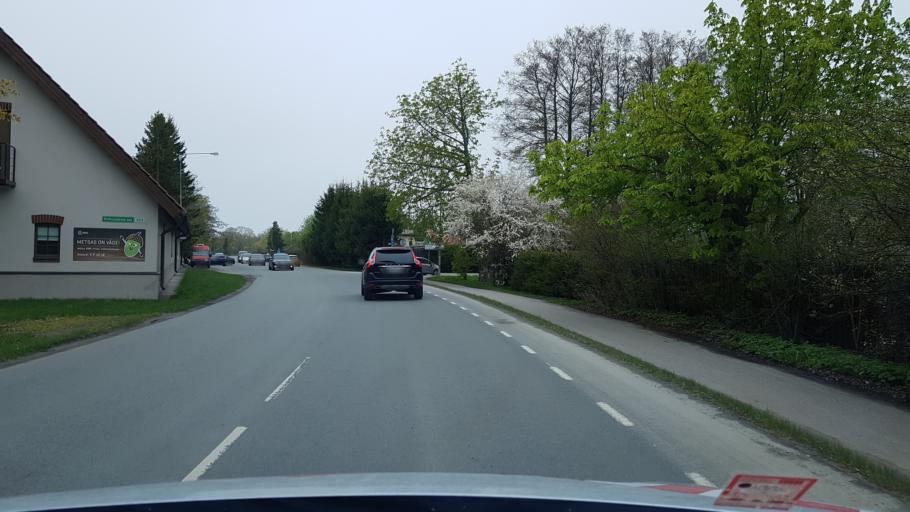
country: EE
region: Harju
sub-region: Viimsi vald
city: Haabneeme
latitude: 59.5152
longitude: 24.8172
